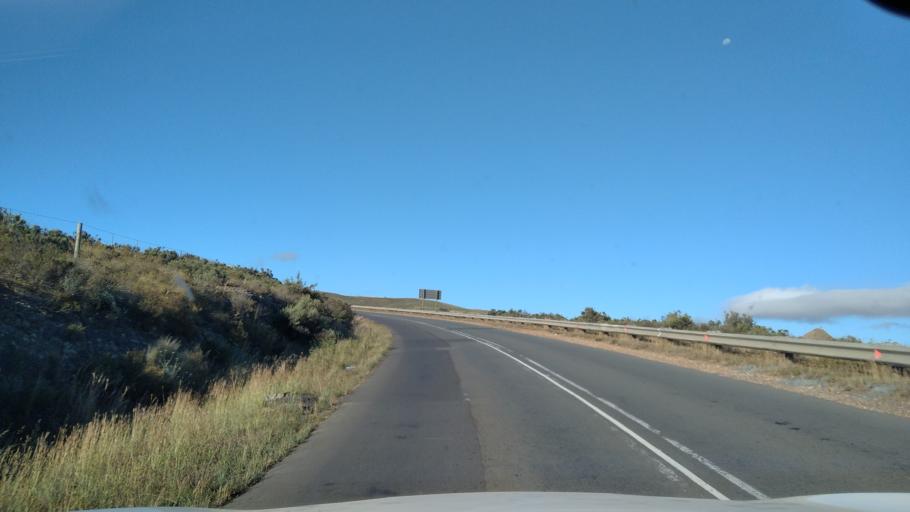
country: ZA
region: Western Cape
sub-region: Overberg District Municipality
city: Caledon
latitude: -34.1588
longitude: 19.3053
